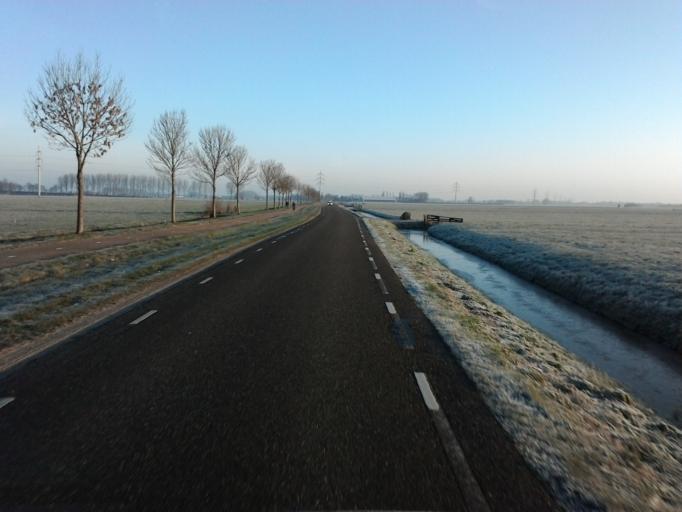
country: NL
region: South Holland
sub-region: Gemeente Gorinchem
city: Gorinchem
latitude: 51.8558
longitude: 4.9604
